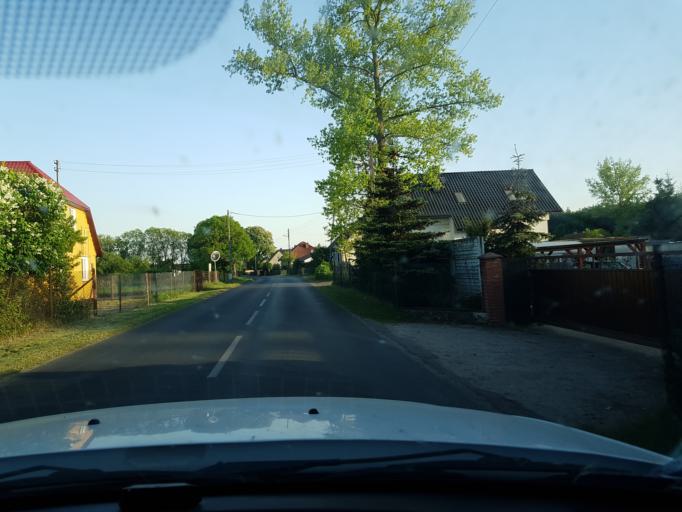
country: PL
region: West Pomeranian Voivodeship
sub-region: Powiat stargardzki
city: Kobylanka
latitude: 53.4276
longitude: 14.9014
